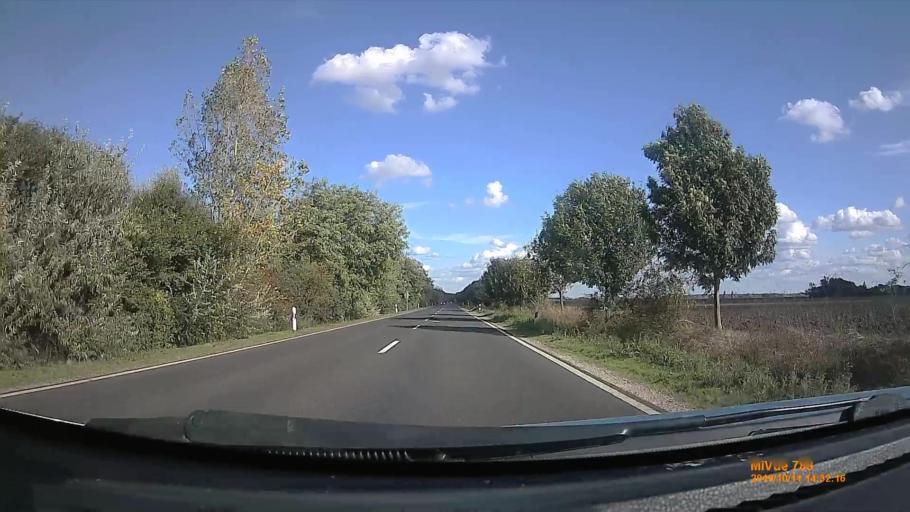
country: HU
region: Hajdu-Bihar
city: Balmazujvaros
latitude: 47.5620
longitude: 21.4345
